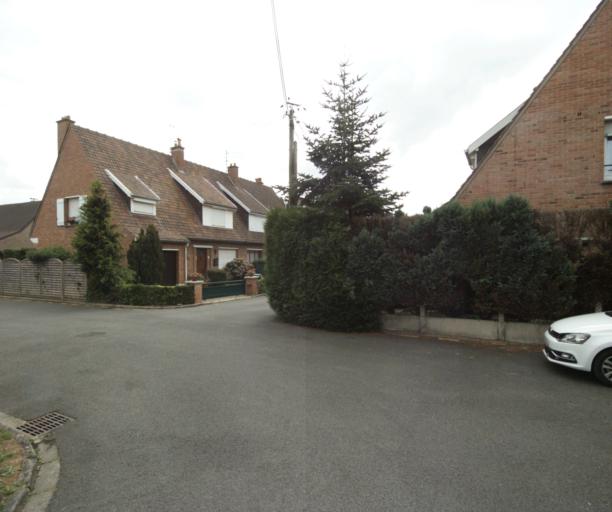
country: FR
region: Nord-Pas-de-Calais
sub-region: Departement du Nord
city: Villeneuve-d'Ascq
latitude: 50.6131
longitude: 3.1619
